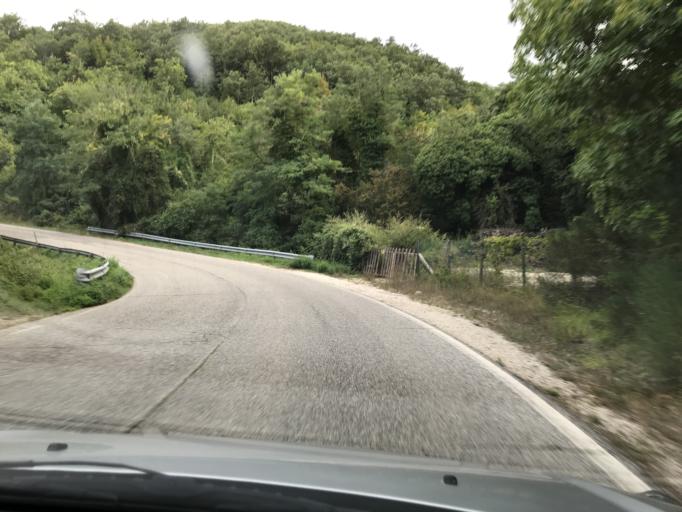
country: IT
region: Umbria
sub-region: Provincia di Terni
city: Montecchio
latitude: 42.6616
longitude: 12.3378
